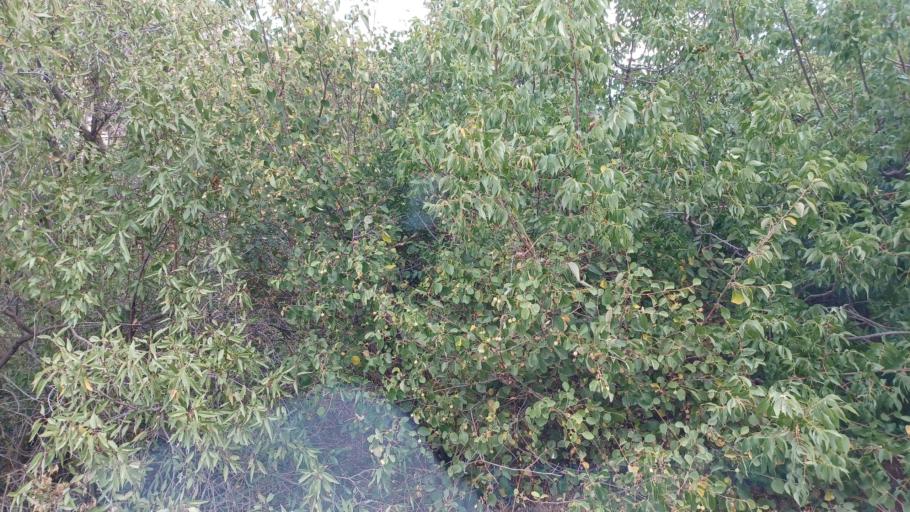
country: CY
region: Limassol
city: Pachna
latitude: 34.8084
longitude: 32.6758
